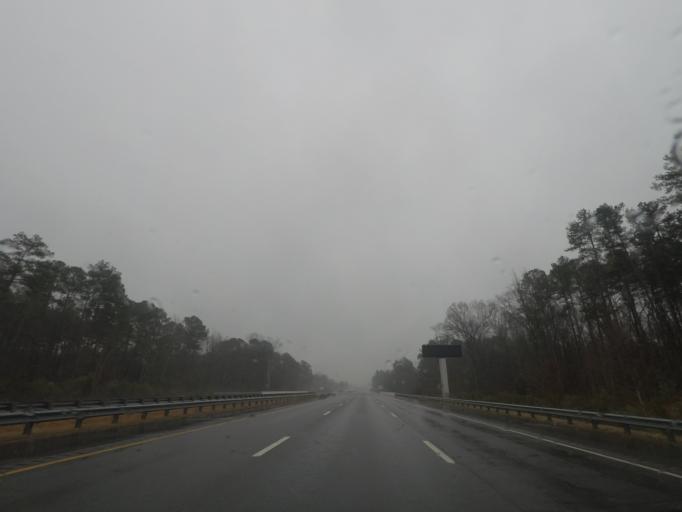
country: US
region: North Carolina
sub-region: Wake County
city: Morrisville
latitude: 35.8927
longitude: -78.8745
